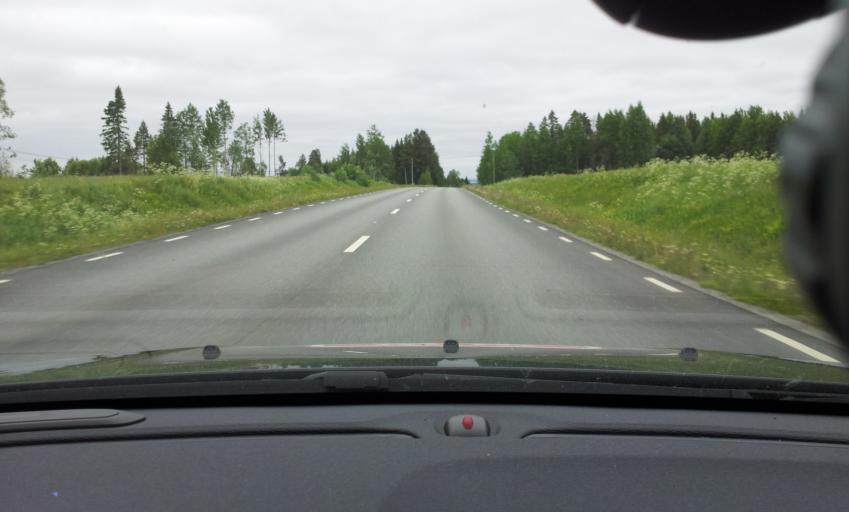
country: SE
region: Jaemtland
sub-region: Krokoms Kommun
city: Krokom
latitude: 63.1126
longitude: 14.2932
